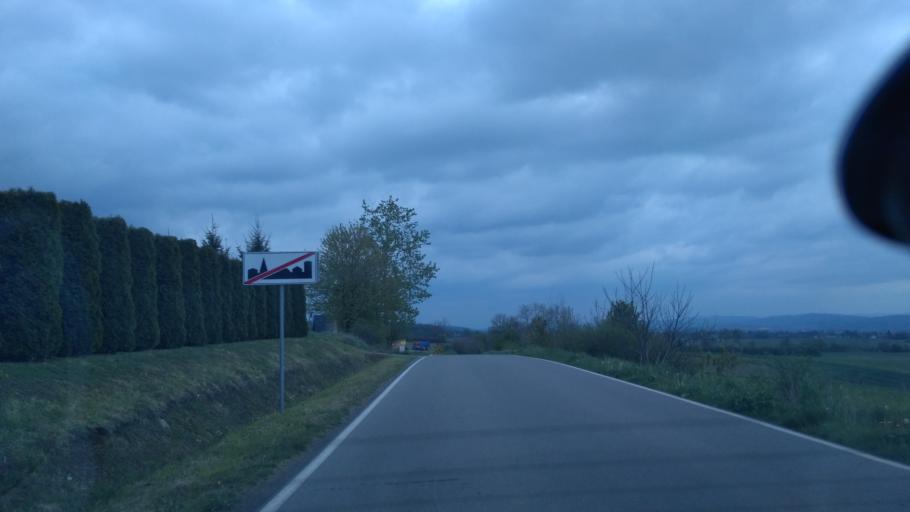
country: PL
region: Subcarpathian Voivodeship
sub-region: Powiat brzozowski
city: Turze Pole
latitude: 49.6387
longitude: 22.0014
